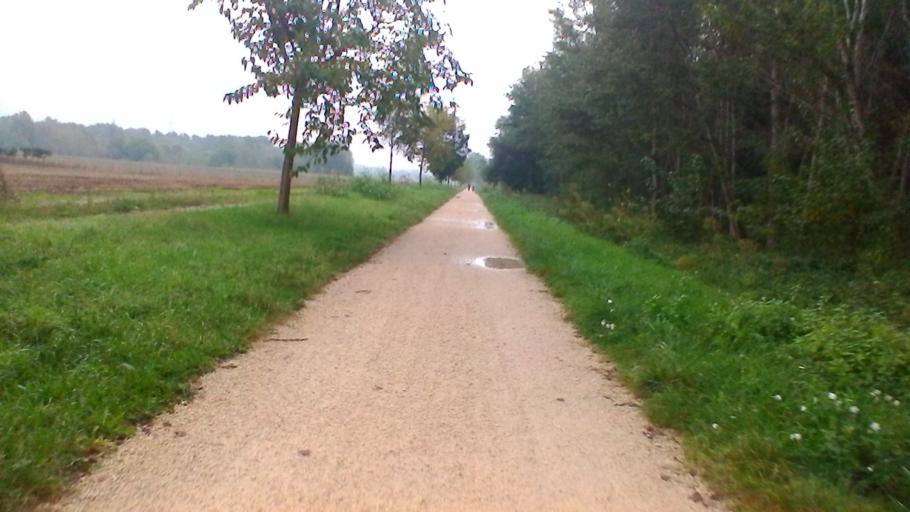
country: IT
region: Veneto
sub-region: Provincia di Verona
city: Verona
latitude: 45.4284
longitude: 11.0242
